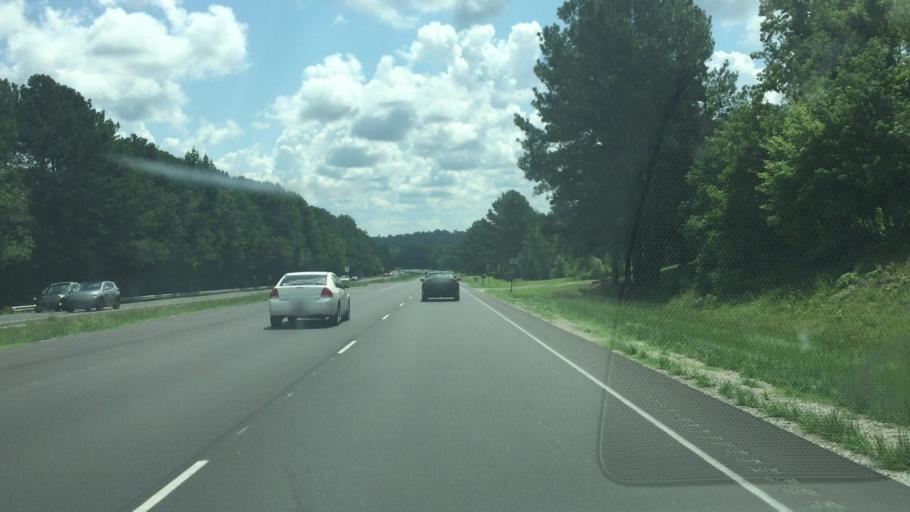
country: US
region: North Carolina
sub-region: Richmond County
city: Cordova
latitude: 34.9464
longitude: -79.8959
